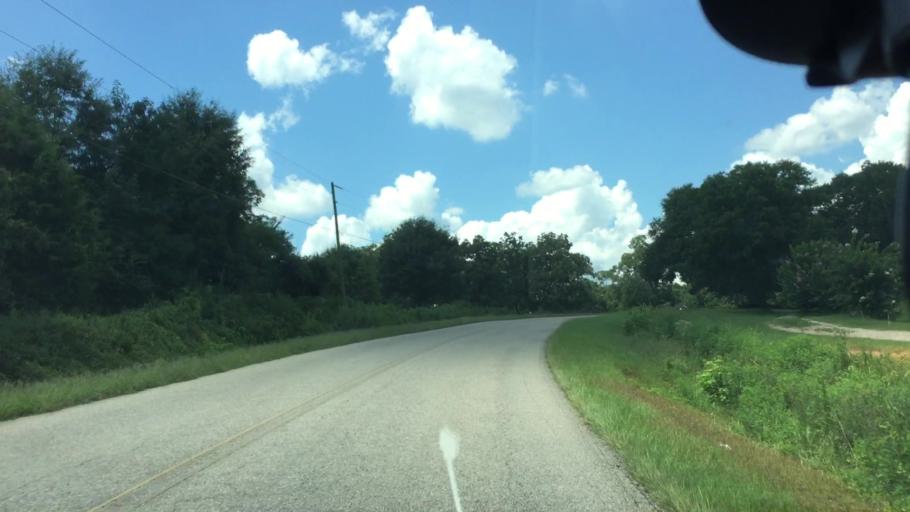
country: US
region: Alabama
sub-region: Pike County
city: Troy
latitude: 31.7512
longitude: -85.9832
